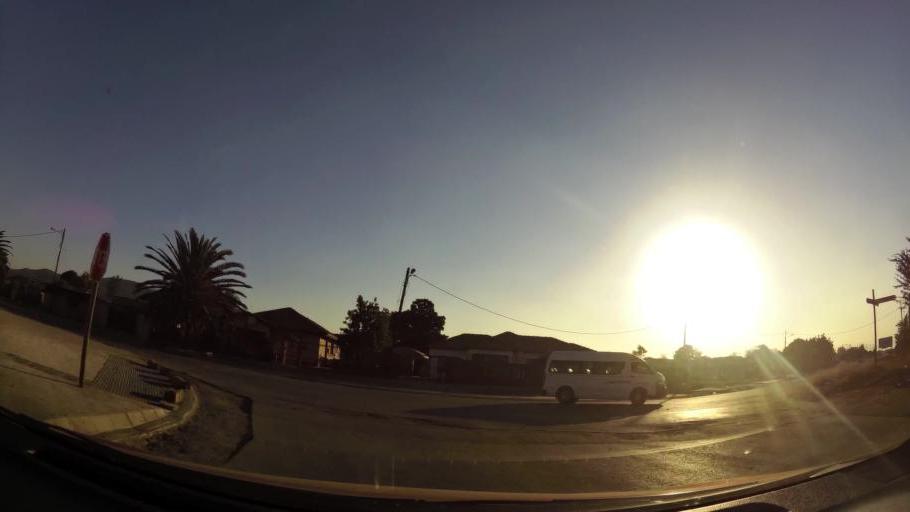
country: ZA
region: North-West
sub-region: Bojanala Platinum District Municipality
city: Rustenburg
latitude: -25.6278
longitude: 27.2154
